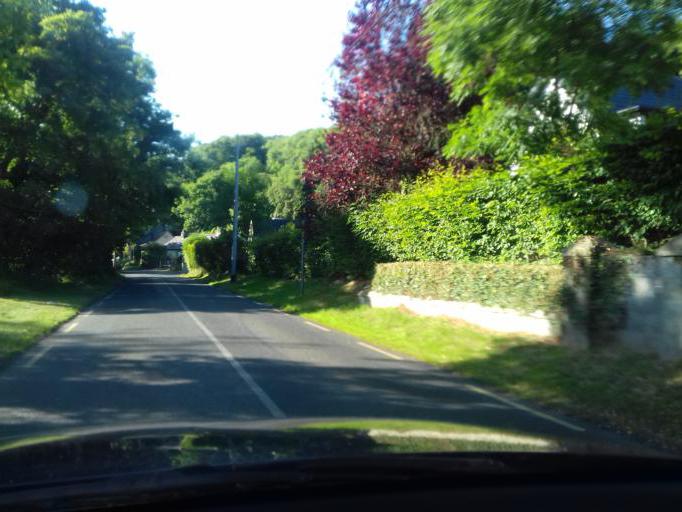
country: IE
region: Leinster
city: Hartstown
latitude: 53.3652
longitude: -6.4098
